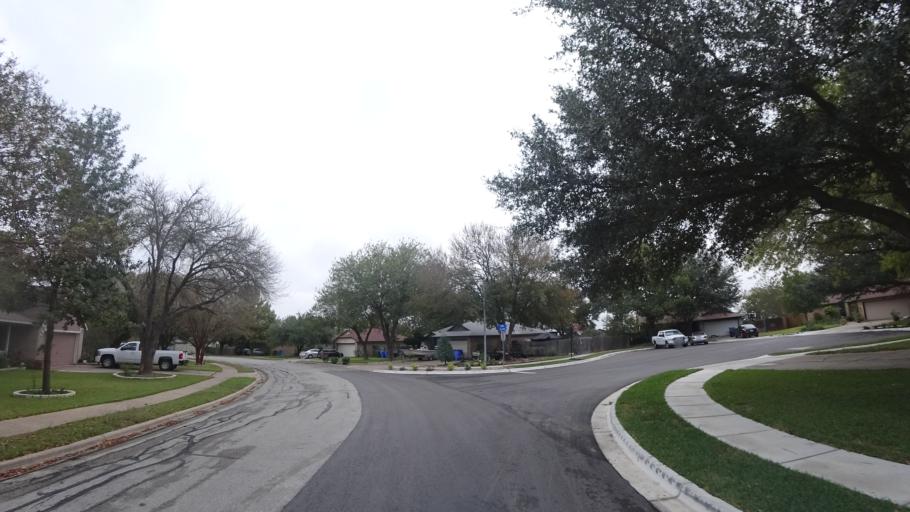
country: US
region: Texas
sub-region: Travis County
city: Pflugerville
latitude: 30.4237
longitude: -97.6101
